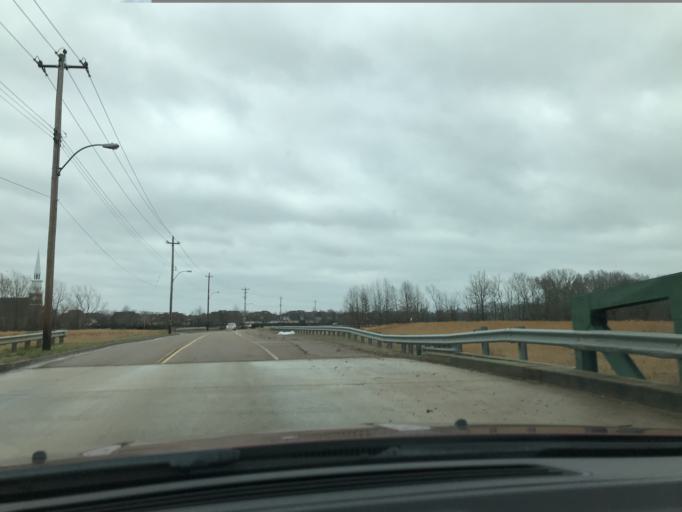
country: US
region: Tennessee
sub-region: Shelby County
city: Collierville
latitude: 35.0908
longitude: -89.7107
